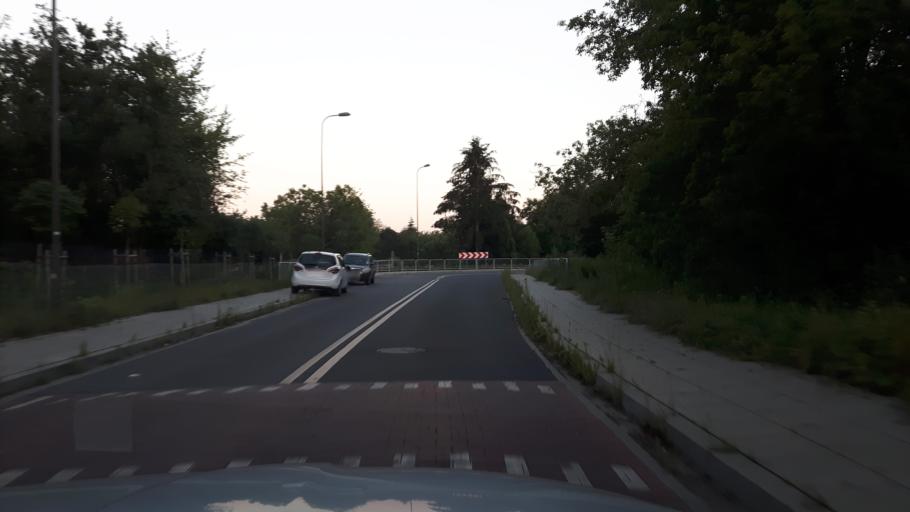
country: PL
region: Masovian Voivodeship
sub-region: Warszawa
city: Mokotow
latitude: 52.2059
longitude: 21.0547
